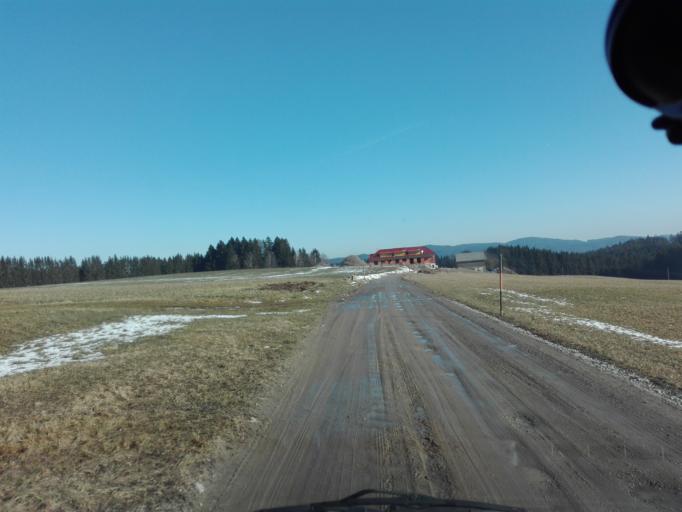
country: AT
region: Upper Austria
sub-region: Politischer Bezirk Urfahr-Umgebung
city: Sonnberg im Muehlkreis
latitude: 48.4615
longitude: 14.3216
